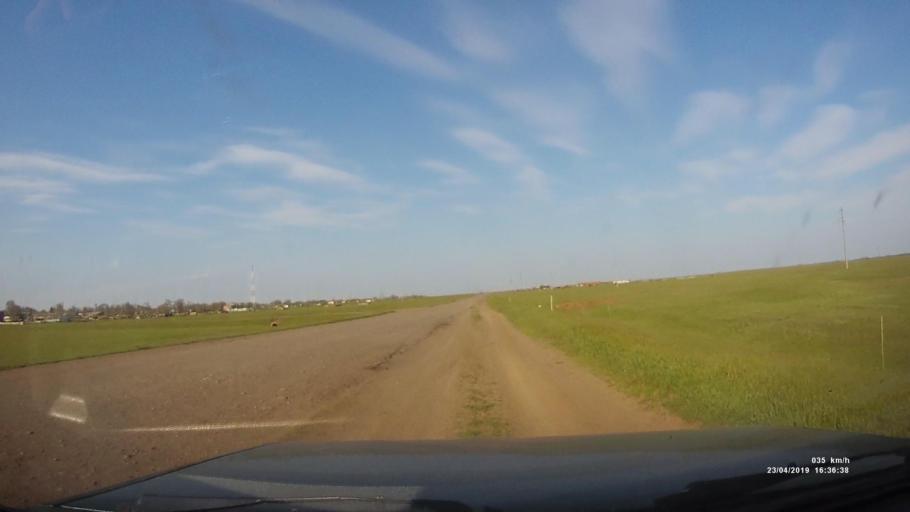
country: RU
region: Kalmykiya
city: Priyutnoye
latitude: 46.3302
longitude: 43.1412
